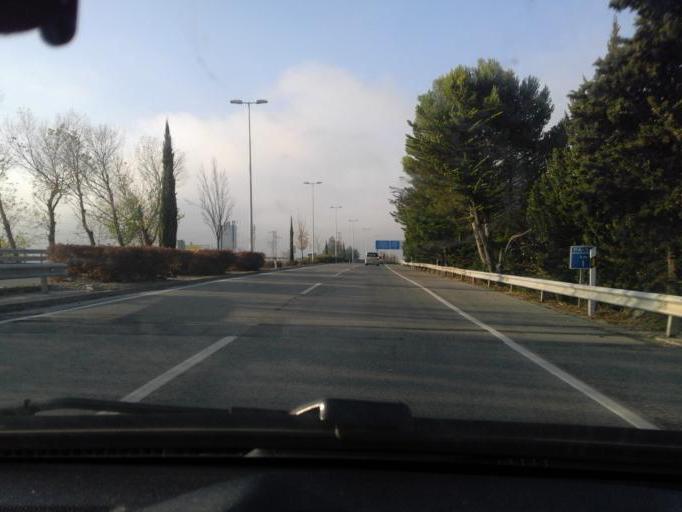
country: ES
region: Navarre
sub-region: Provincia de Navarra
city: Berriozar
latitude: 42.8367
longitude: -1.6786
